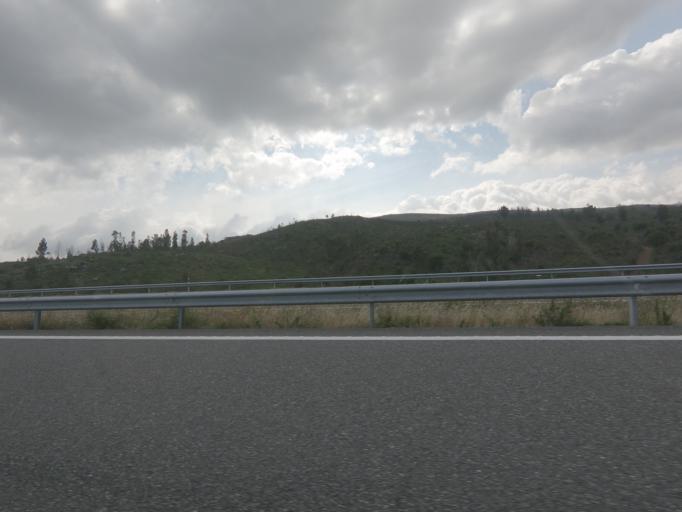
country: ES
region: Galicia
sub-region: Provincia de Ourense
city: Melon
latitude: 42.2780
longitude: -8.2033
